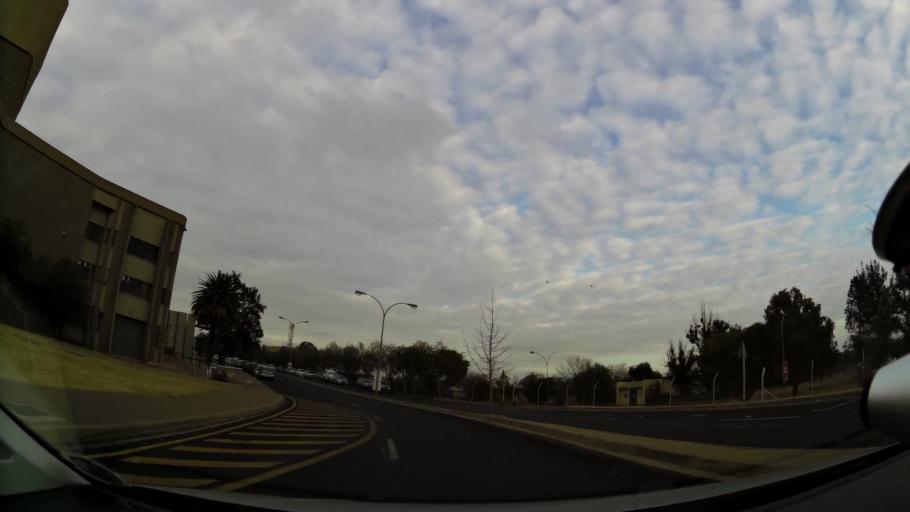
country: ZA
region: Orange Free State
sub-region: Mangaung Metropolitan Municipality
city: Bloemfontein
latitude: -29.1079
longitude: 26.1858
